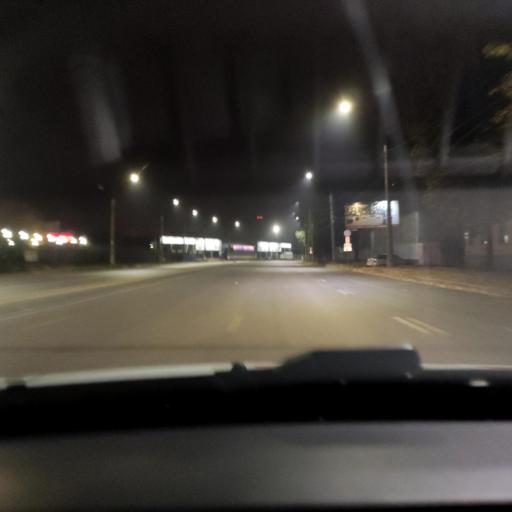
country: RU
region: Voronezj
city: Voronezh
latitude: 51.6791
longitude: 39.1751
